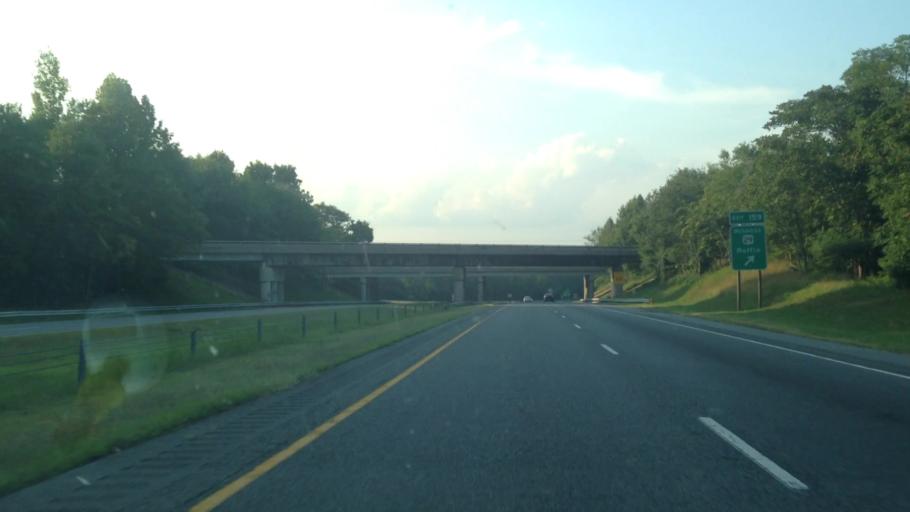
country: US
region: North Carolina
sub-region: Rockingham County
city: Reidsville
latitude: 36.4327
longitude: -79.5725
